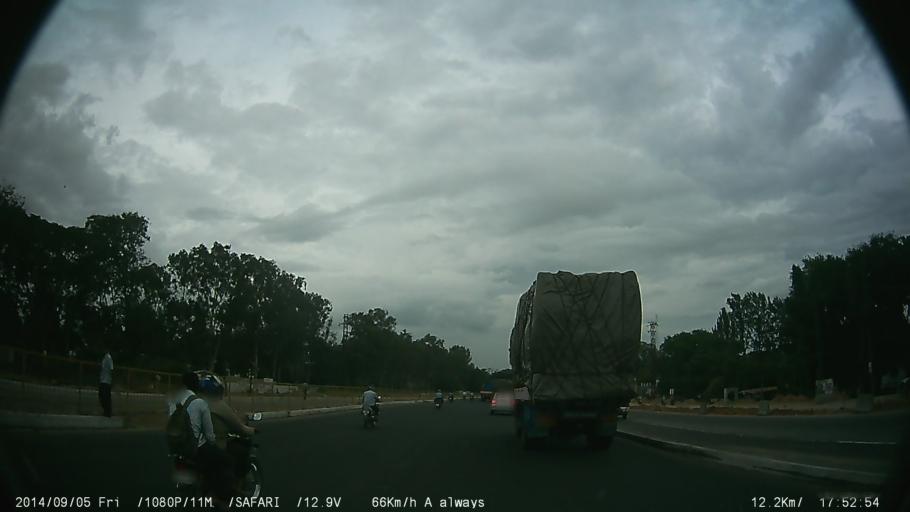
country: IN
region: Tamil Nadu
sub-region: Krishnagiri
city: Hosur
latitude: 12.7578
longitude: 77.7993
